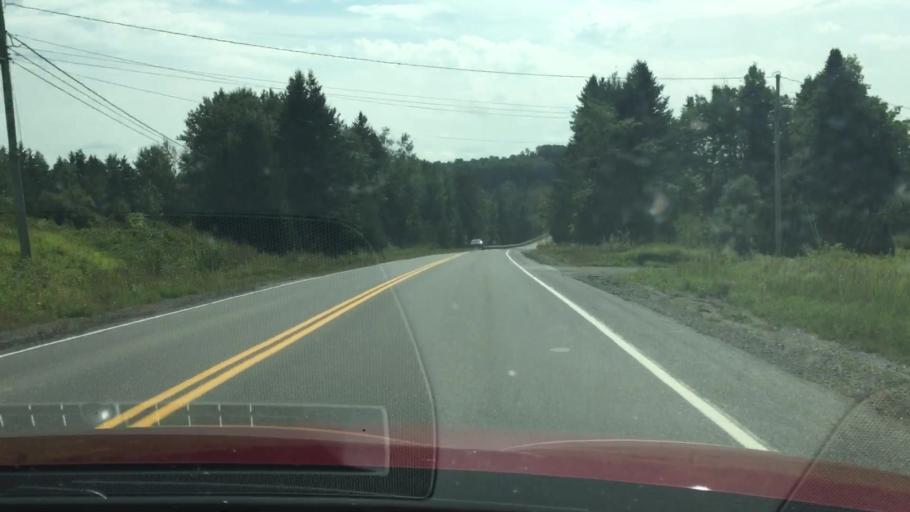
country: US
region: Maine
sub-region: Aroostook County
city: Easton
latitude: 46.6018
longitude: -67.9705
